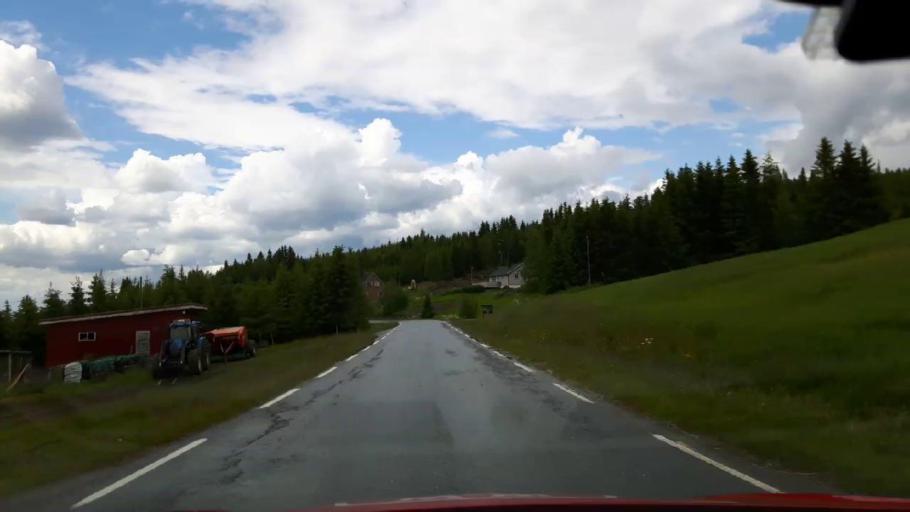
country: NO
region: Nord-Trondelag
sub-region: Lierne
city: Sandvika
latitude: 64.1089
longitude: 13.9817
